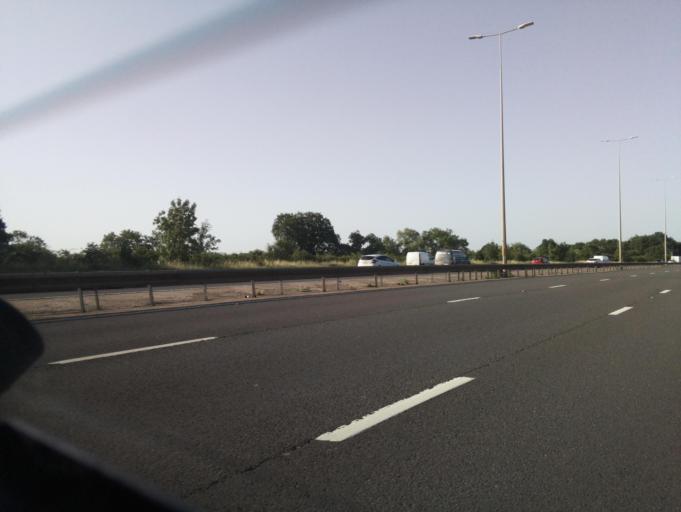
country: GB
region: England
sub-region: Worcestershire
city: Fernhill Heath
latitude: 52.2027
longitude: -2.1630
